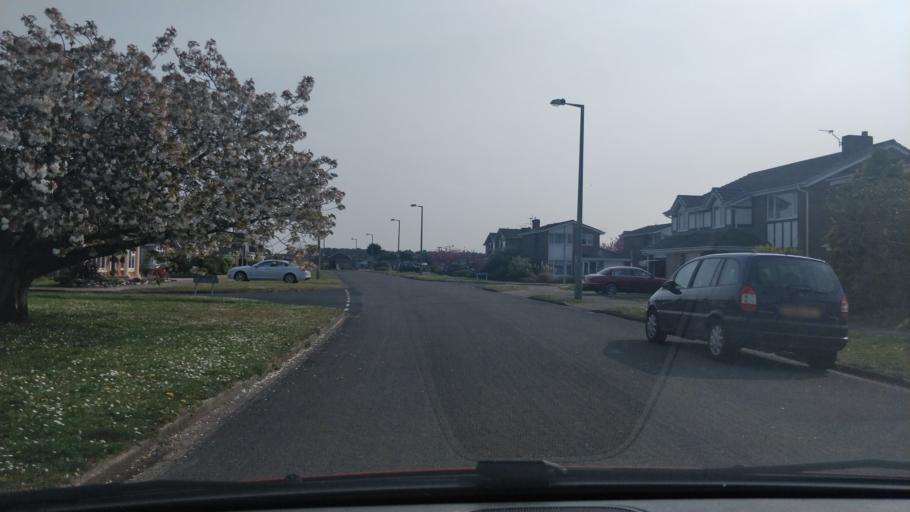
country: GB
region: England
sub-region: Sefton
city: Formby
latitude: 53.6024
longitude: -3.0535
